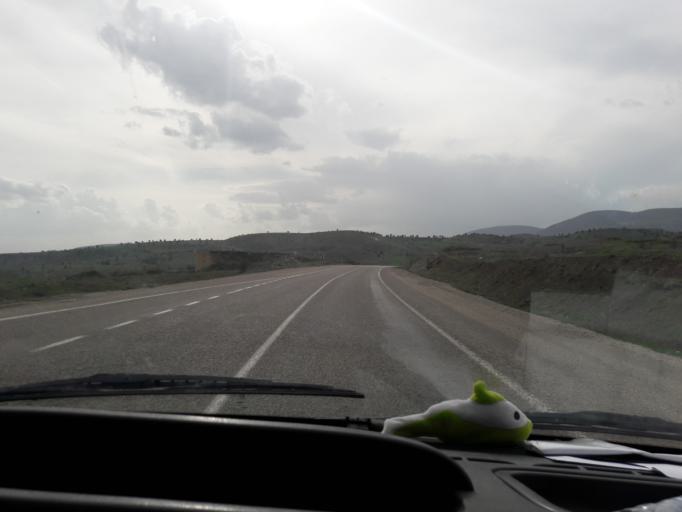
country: TR
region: Gumushane
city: Siran
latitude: 40.1601
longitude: 39.0162
